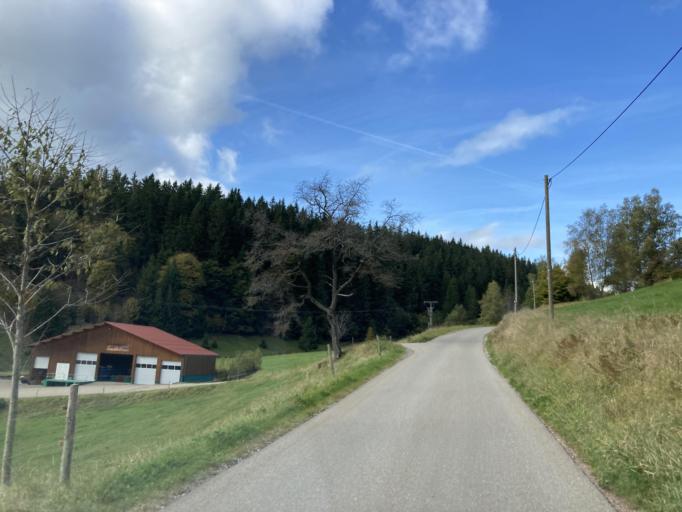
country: DE
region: Baden-Wuerttemberg
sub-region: Freiburg Region
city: Vohrenbach
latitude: 48.0656
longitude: 8.2839
